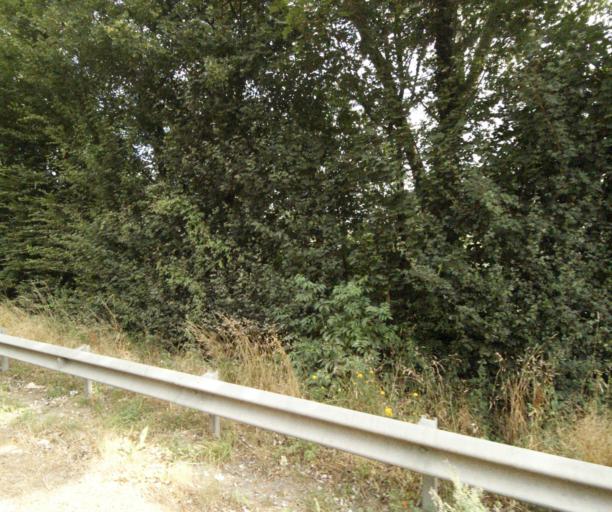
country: FR
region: Nord-Pas-de-Calais
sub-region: Departement du Nord
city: Santes
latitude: 50.5998
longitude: 2.9771
